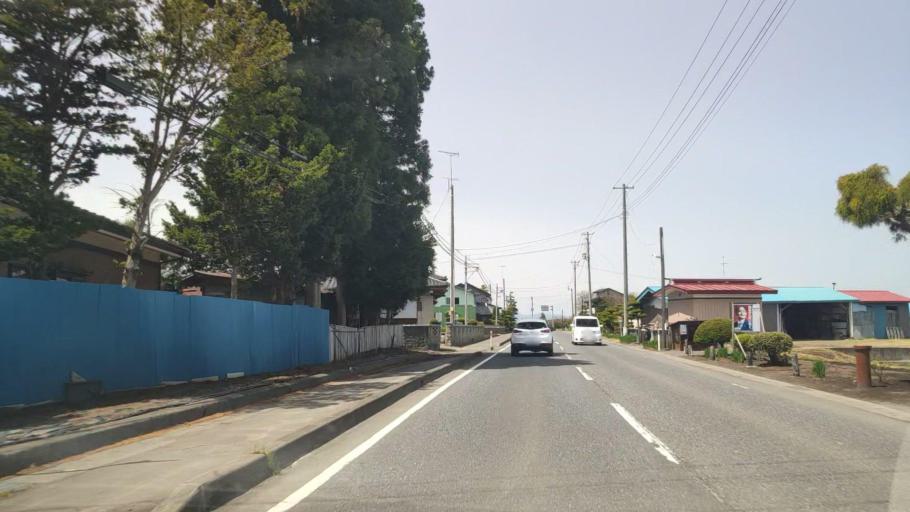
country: JP
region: Aomori
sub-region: Misawa Shi
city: Inuotose
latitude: 40.5918
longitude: 141.3472
